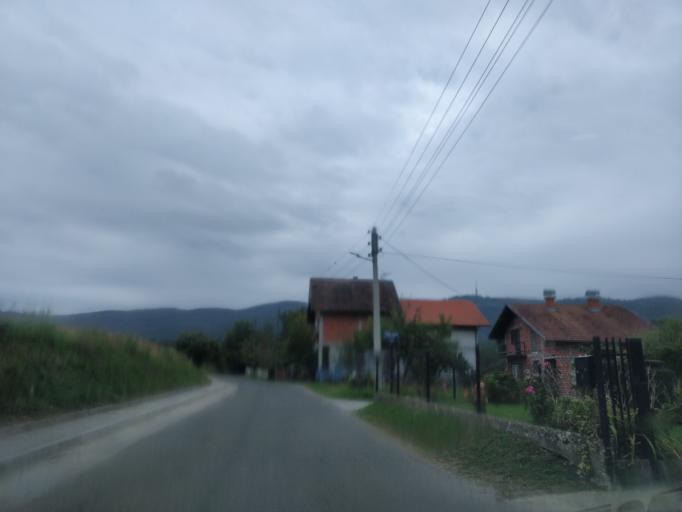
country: HR
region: Krapinsko-Zagorska
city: Oroslavje
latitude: 45.9422
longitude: 15.9198
